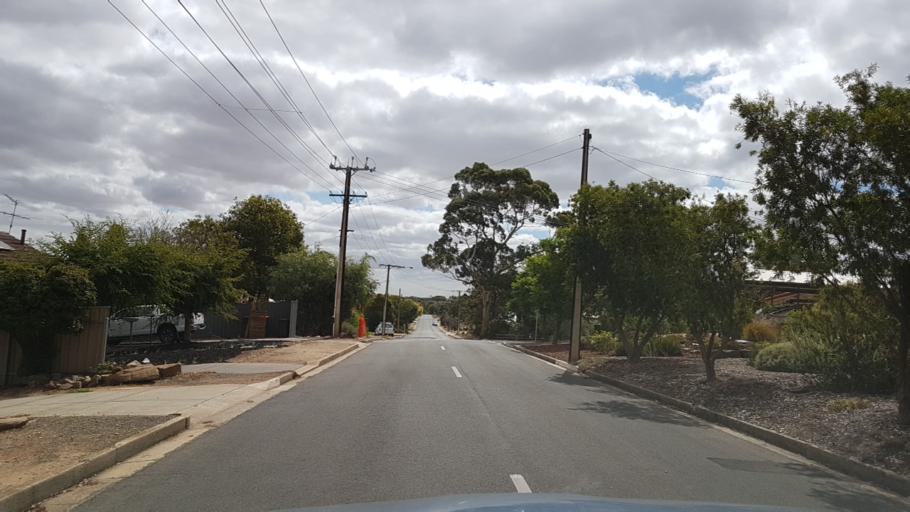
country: AU
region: South Australia
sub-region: Gawler
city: Gawler
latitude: -34.6096
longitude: 138.7545
